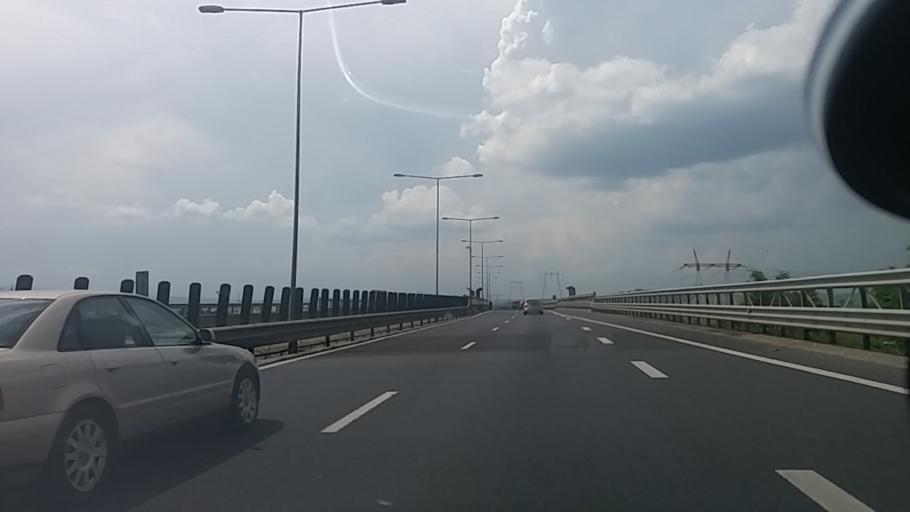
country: RO
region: Sibiu
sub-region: Municipiul Sibiu
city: Sibiu
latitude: 45.8231
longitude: 24.1529
